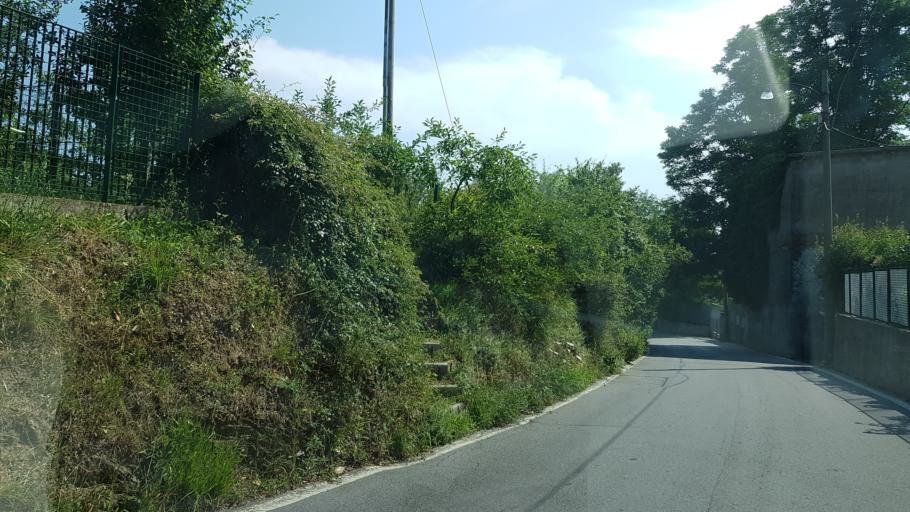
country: IT
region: Liguria
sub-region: Provincia di Genova
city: Genoa
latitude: 44.4406
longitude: 8.8949
